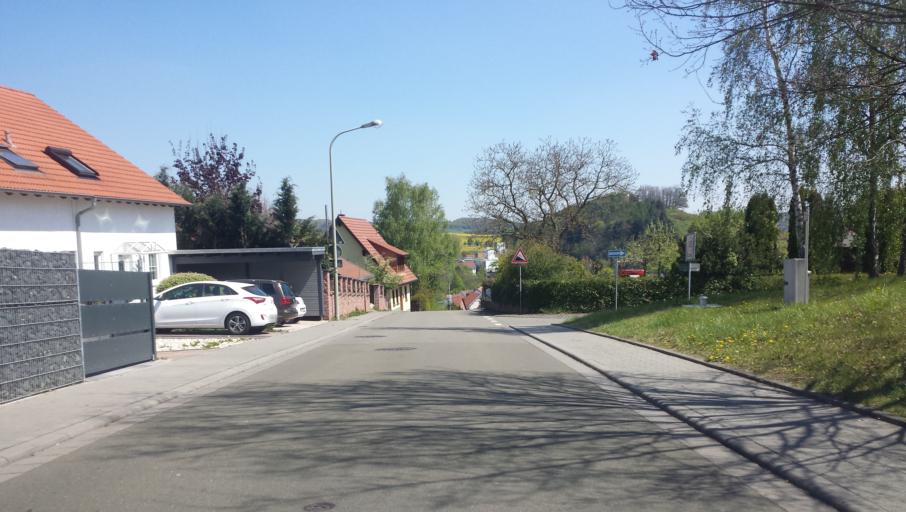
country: DE
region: Rheinland-Pfalz
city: Winnweiler
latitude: 49.5697
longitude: 7.8488
